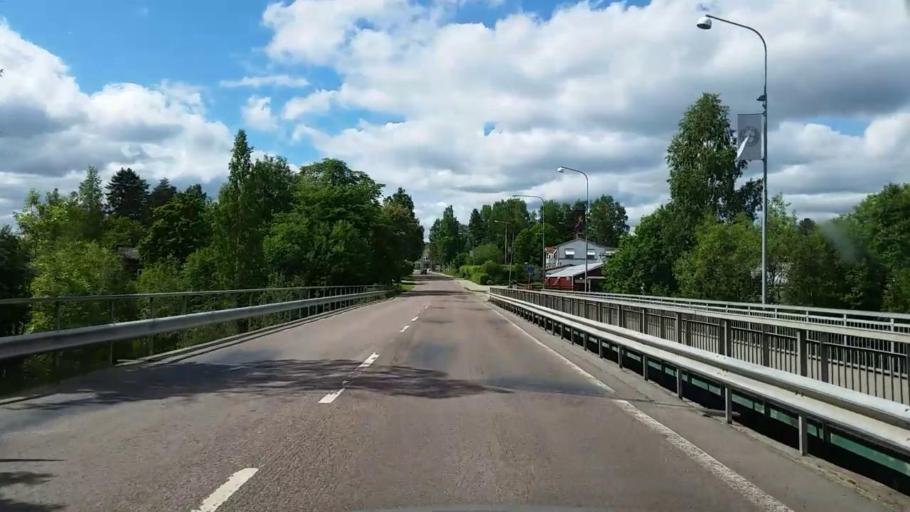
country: SE
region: Gaevleborg
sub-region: Ovanakers Kommun
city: Alfta
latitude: 61.3446
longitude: 16.0599
